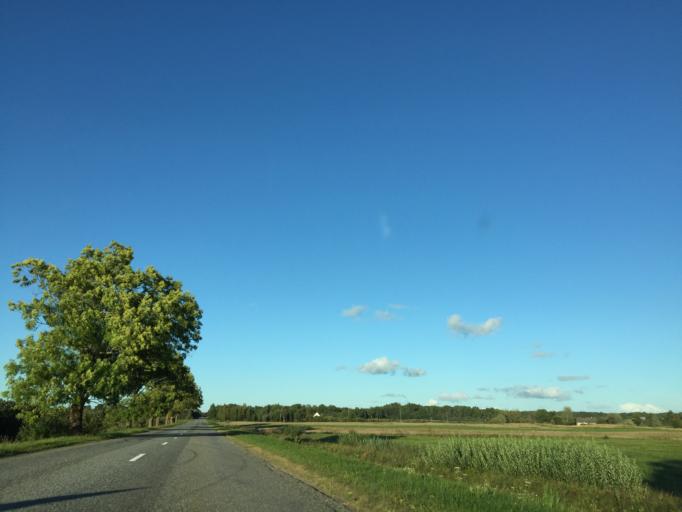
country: LV
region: Kuldigas Rajons
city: Kuldiga
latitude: 56.9736
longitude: 22.0008
